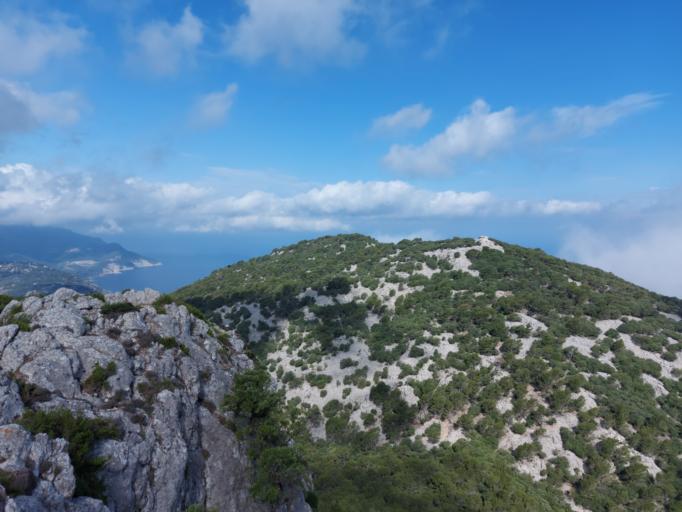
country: ES
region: Balearic Islands
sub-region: Illes Balears
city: Valldemossa
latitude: 39.7278
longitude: 2.6249
